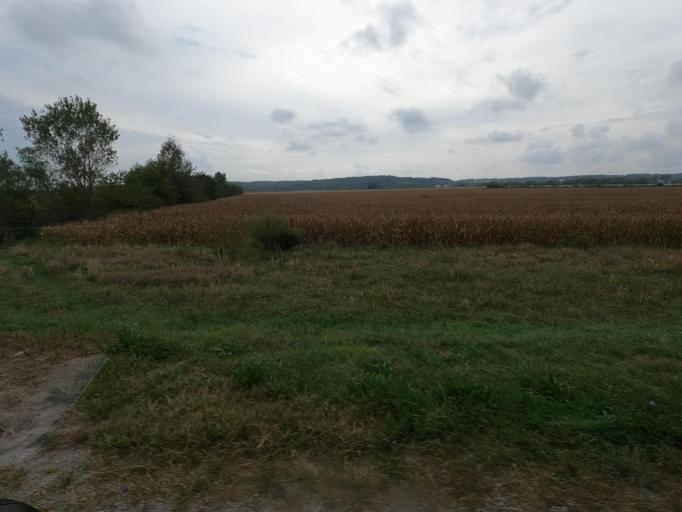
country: US
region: Iowa
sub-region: Wapello County
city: Ottumwa
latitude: 40.9024
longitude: -92.1973
